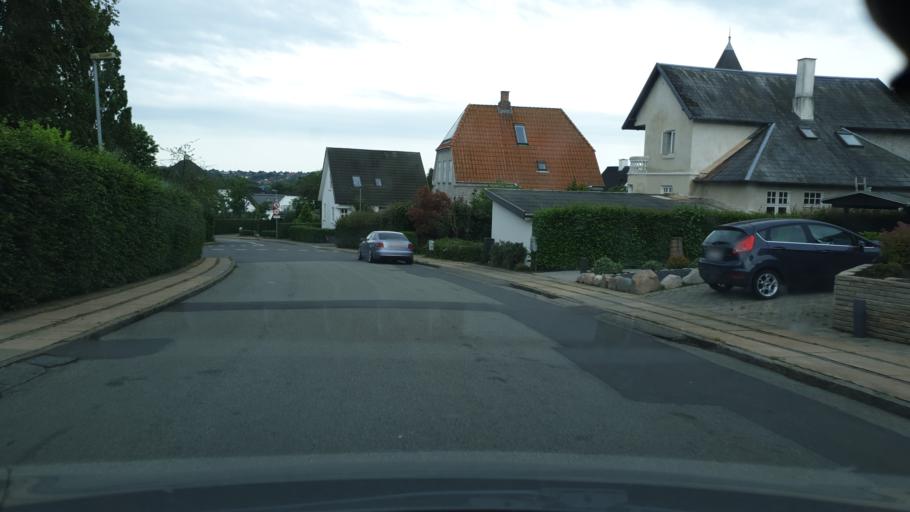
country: DK
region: South Denmark
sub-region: Kolding Kommune
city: Kolding
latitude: 55.4991
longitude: 9.4931
